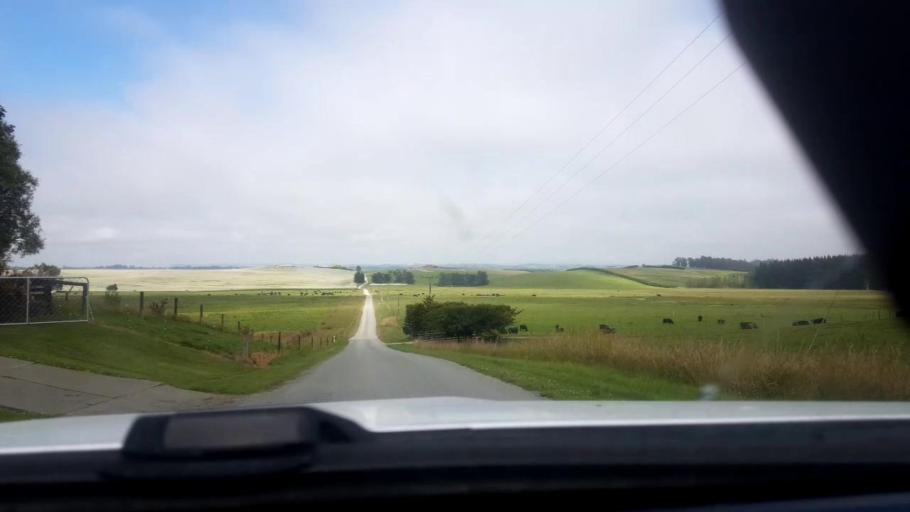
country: NZ
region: Canterbury
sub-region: Timaru District
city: Timaru
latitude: -44.3272
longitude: 171.2095
